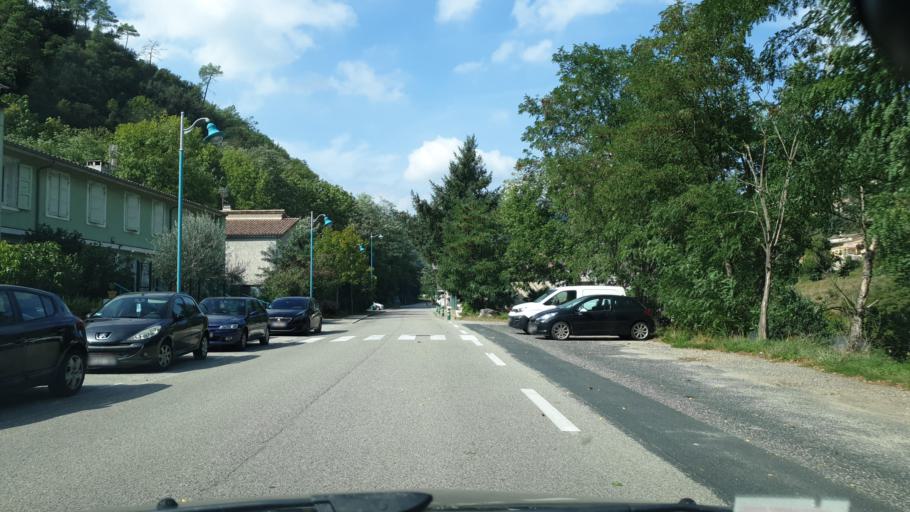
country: FR
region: Rhone-Alpes
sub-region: Departement de l'Ardeche
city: Saint-Sauveur-de-Montagut
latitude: 44.8186
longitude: 4.5938
